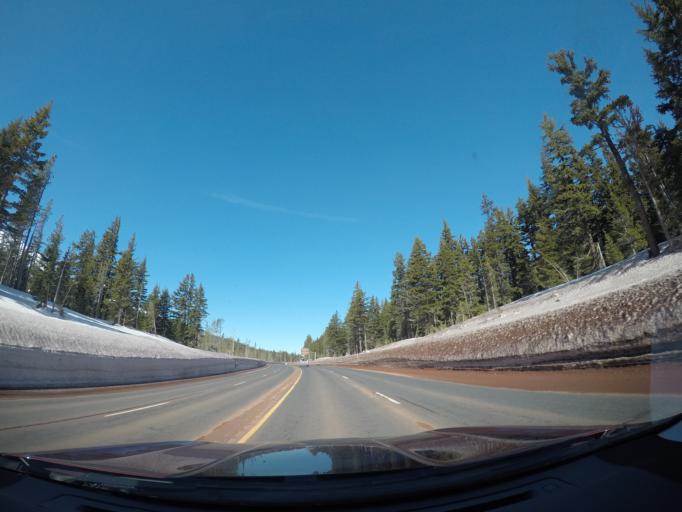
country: US
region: Oregon
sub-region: Deschutes County
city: Sunriver
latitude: 43.9895
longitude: -121.6512
